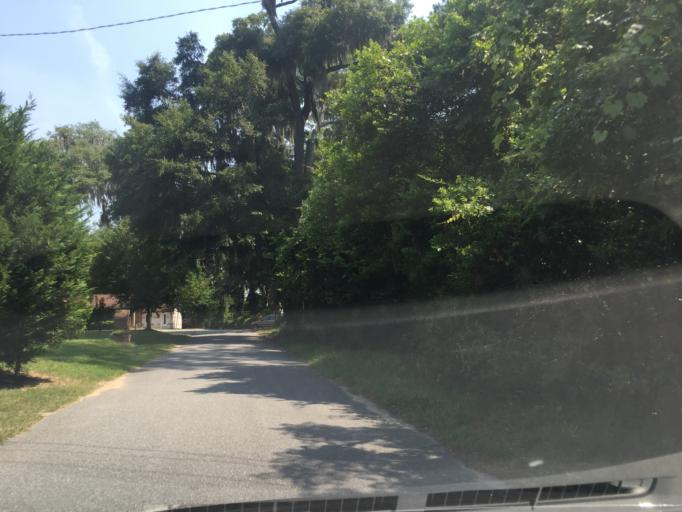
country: US
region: Georgia
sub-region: Chatham County
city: Montgomery
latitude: 31.9664
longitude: -81.1260
